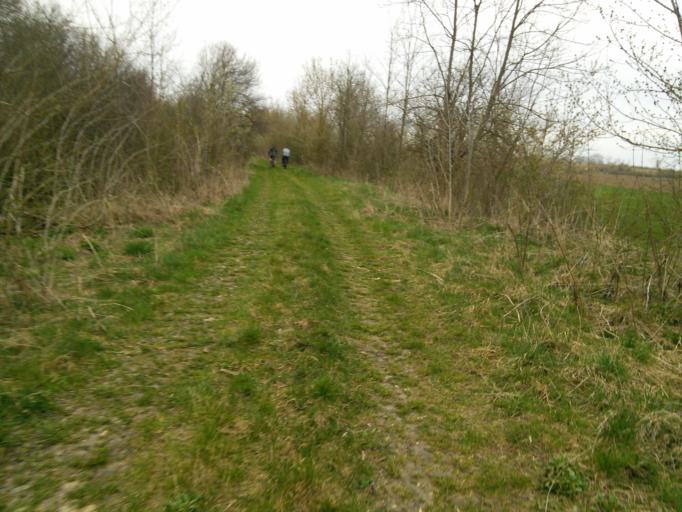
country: HU
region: Tolna
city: Dombovar
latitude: 46.4082
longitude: 18.1831
